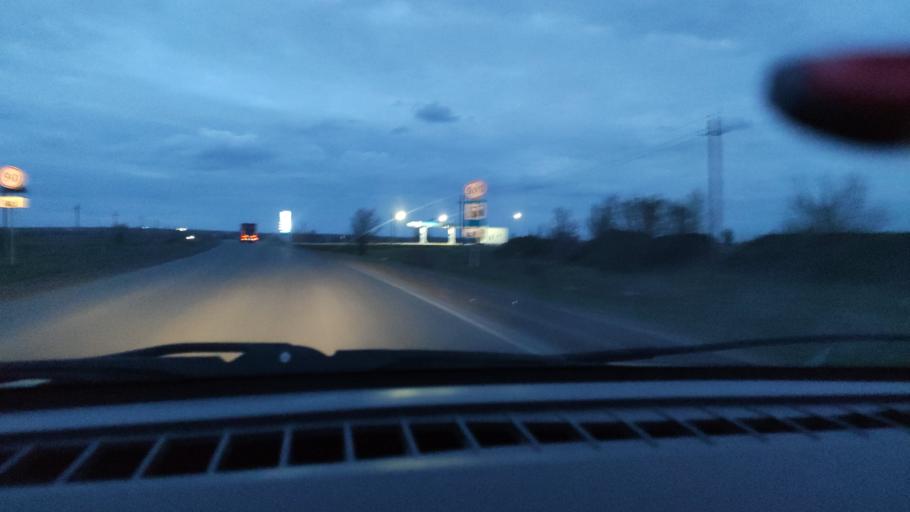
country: RU
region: Orenburg
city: Tatarskaya Kargala
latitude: 51.9050
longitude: 55.1711
